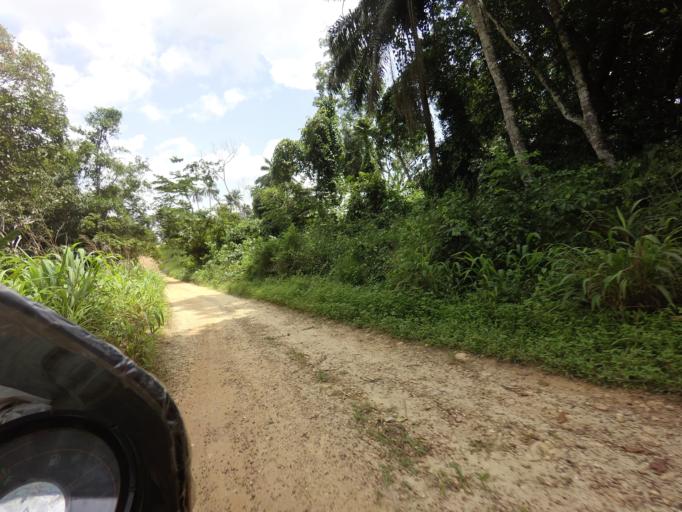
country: SL
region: Eastern Province
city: Kailahun
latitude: 8.3686
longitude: -10.7145
